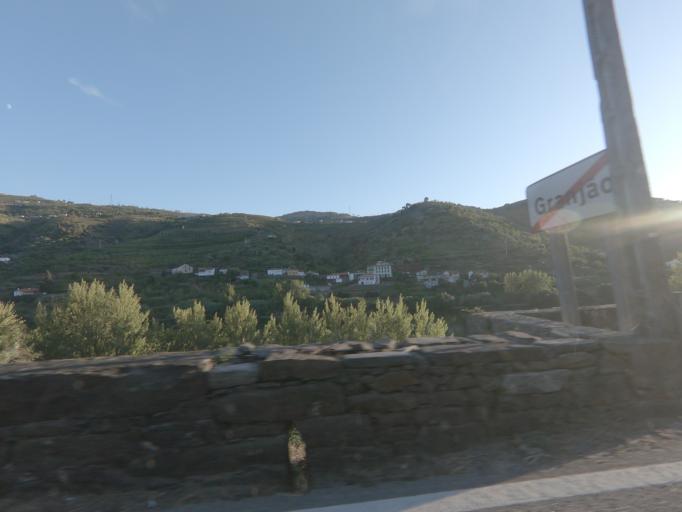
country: PT
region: Vila Real
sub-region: Mesao Frio
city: Mesao Frio
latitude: 41.1580
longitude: -7.8536
